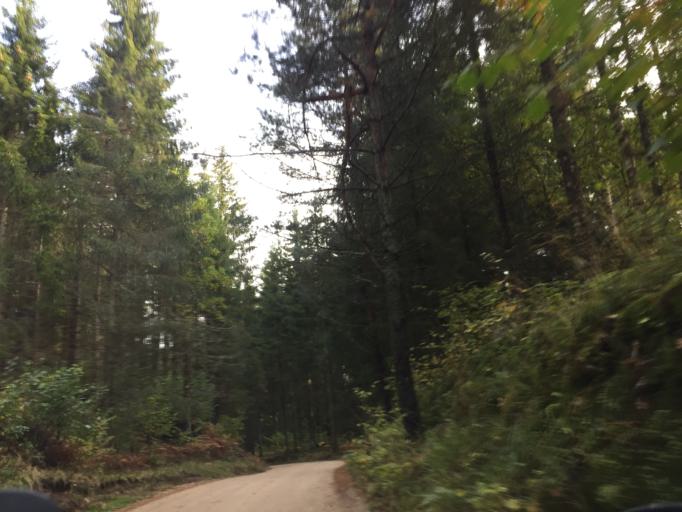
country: LV
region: Jaunpils
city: Jaunpils
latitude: 56.5841
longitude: 23.0143
